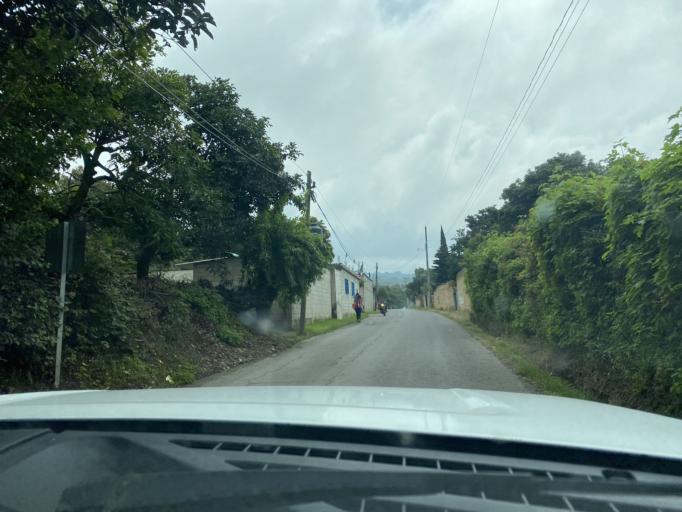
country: MX
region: Morelos
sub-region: Yecapixtla
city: Texcala
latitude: 18.9331
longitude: -98.7987
